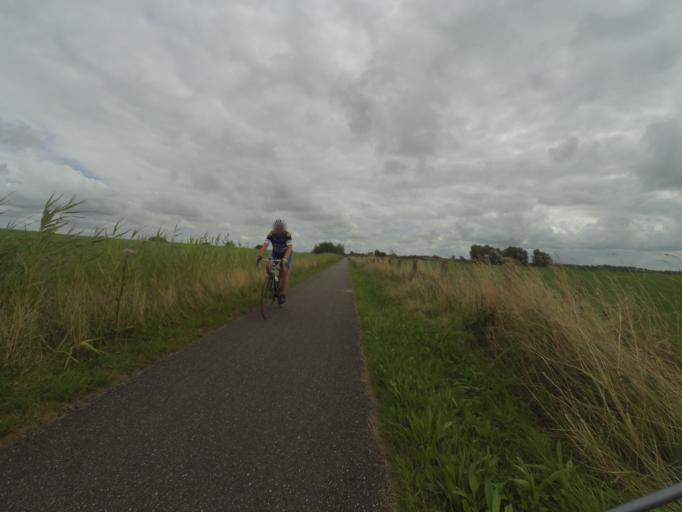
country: NL
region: Friesland
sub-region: Gemeente Kollumerland en Nieuwkruisland
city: Kollumerzwaag
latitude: 53.2954
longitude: 6.1009
